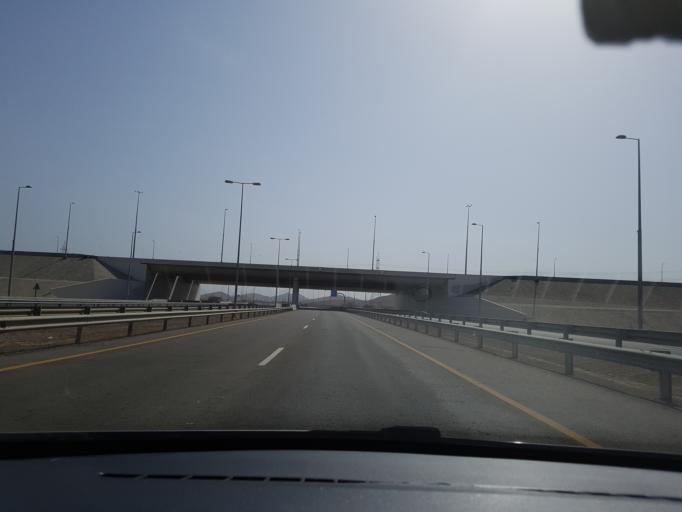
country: OM
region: Al Batinah
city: Al Liwa'
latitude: 24.3866
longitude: 56.5528
